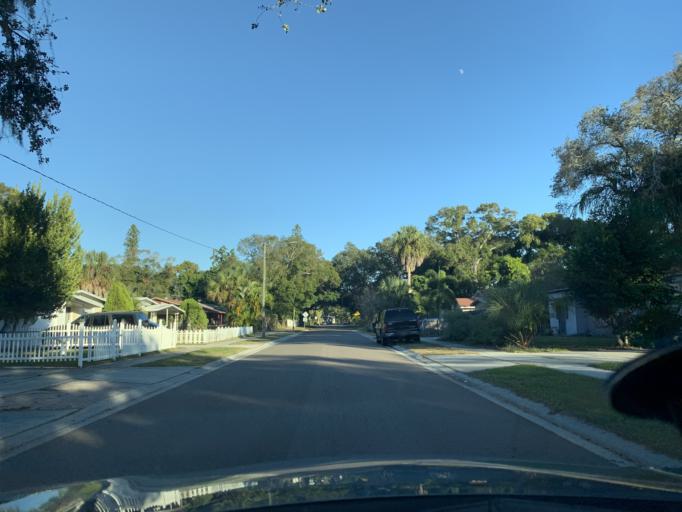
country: US
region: Florida
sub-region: Pinellas County
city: Gulfport
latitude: 27.7475
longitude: -82.6973
